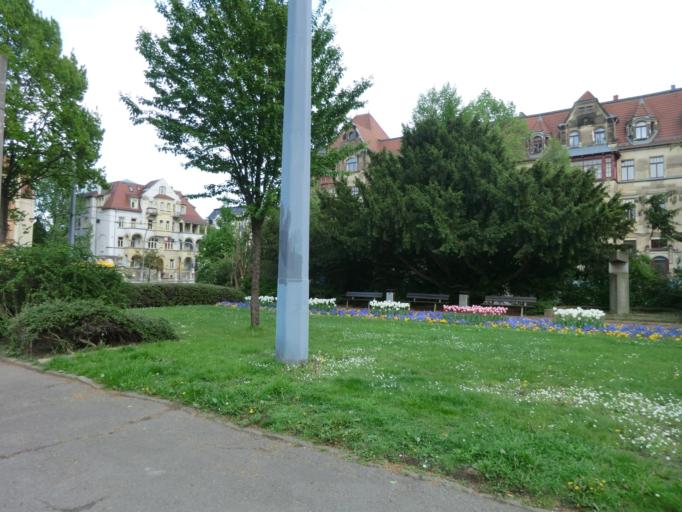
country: DE
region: Saxony
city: Dresden
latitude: 51.0465
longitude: 13.7715
